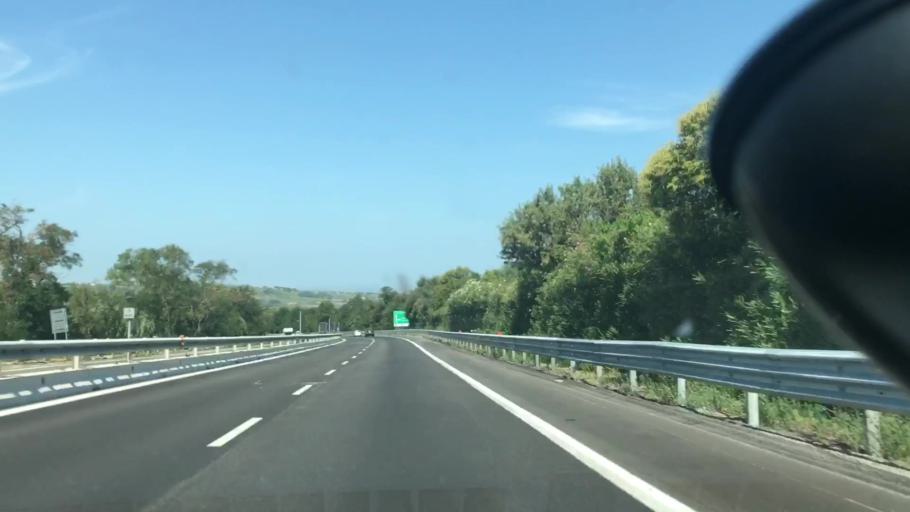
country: IT
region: Abruzzo
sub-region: Provincia di Chieti
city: Casalbordino-Miracoli
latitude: 42.1506
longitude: 14.6534
